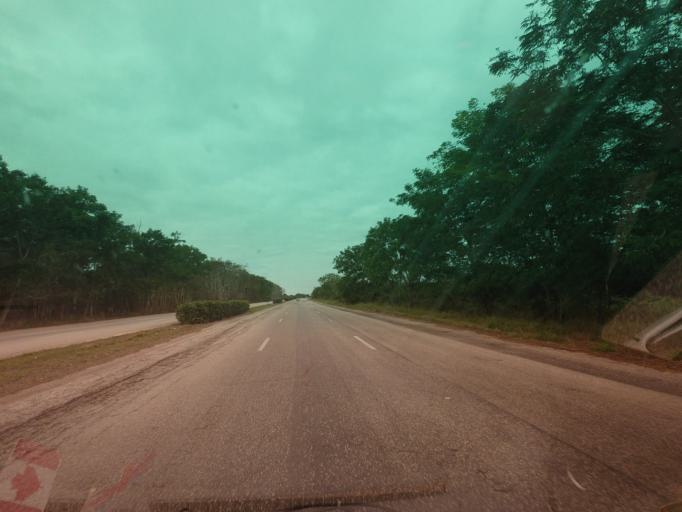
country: CU
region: Mayabeque
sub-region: Municipio de San Nicolas
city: San Nicolas de Bari
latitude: 22.7931
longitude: -81.8547
